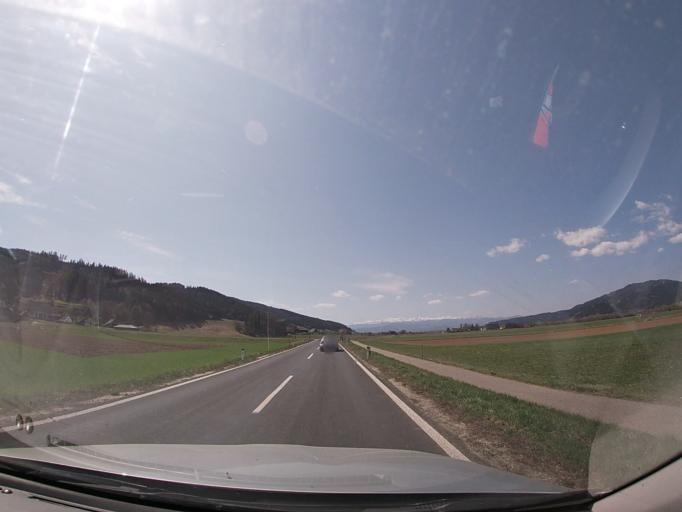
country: AT
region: Styria
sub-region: Politischer Bezirk Murtal
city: Sankt Lorenzen bei Knittelfeld
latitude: 47.2472
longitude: 14.8891
